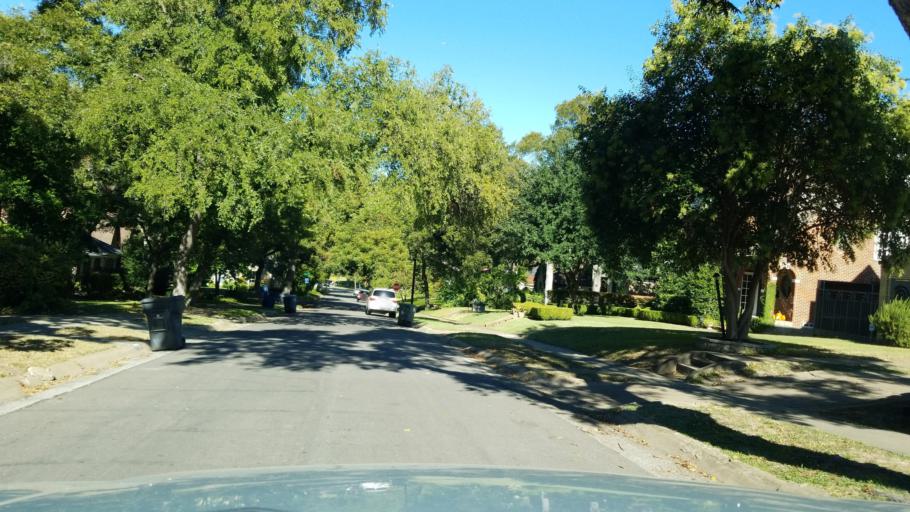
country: US
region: Texas
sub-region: Dallas County
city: Highland Park
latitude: 32.8069
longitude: -96.7409
